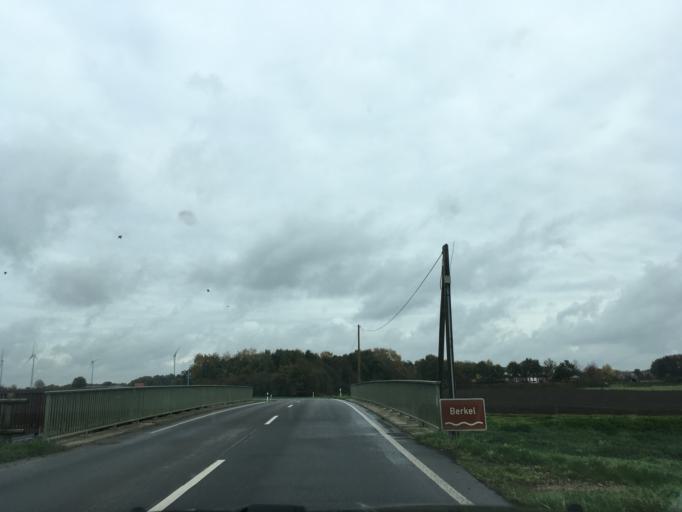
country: DE
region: North Rhine-Westphalia
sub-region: Regierungsbezirk Munster
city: Vreden
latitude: 52.0801
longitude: 6.7746
